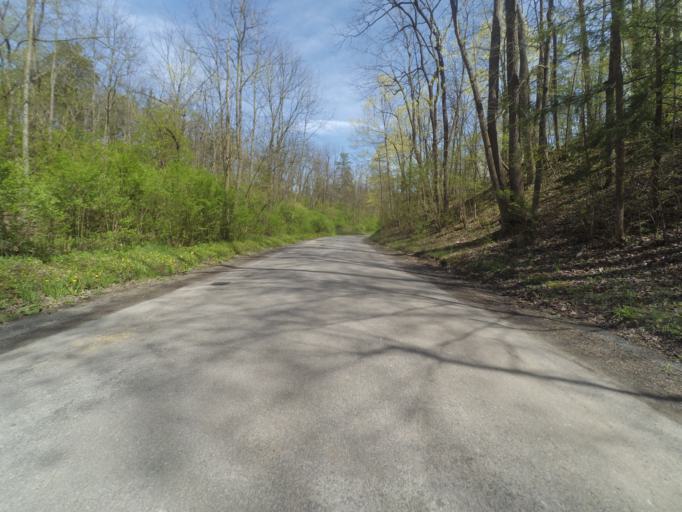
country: US
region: Pennsylvania
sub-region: Blair County
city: Tyrone
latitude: 40.6021
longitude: -78.2155
